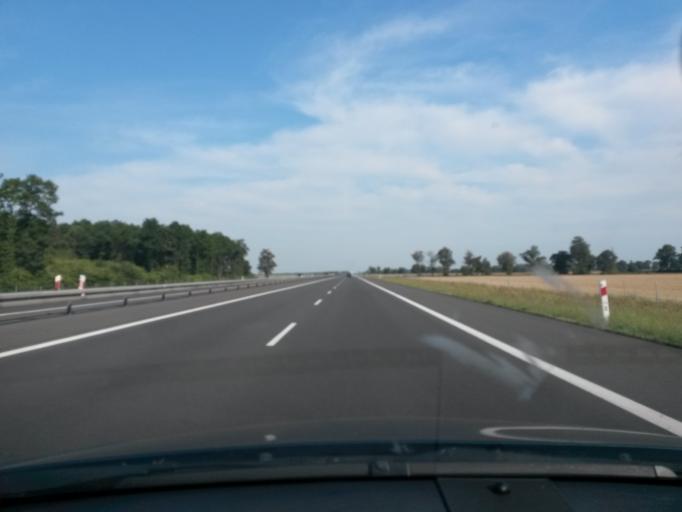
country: PL
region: Greater Poland Voivodeship
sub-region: Powiat wrzesinski
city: Wrzesnia
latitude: 52.3043
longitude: 17.6092
